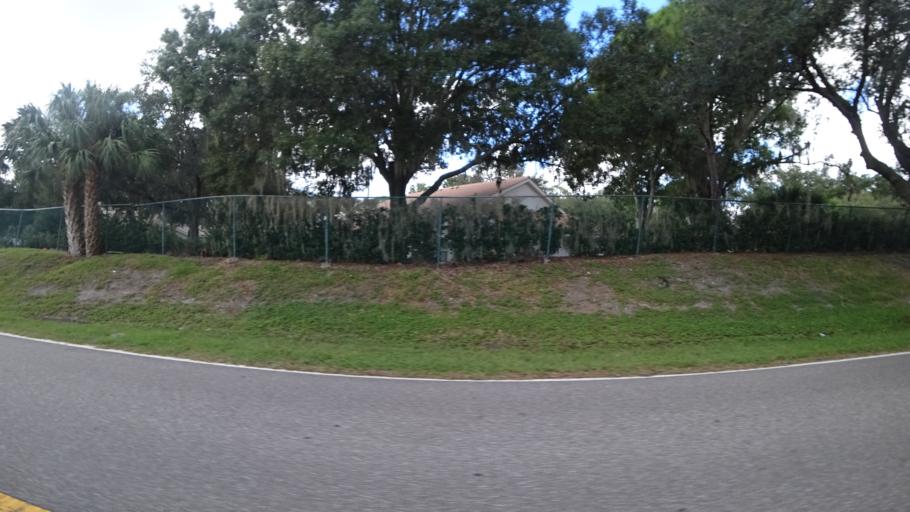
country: US
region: Florida
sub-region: Manatee County
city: Samoset
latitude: 27.4384
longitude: -82.5136
